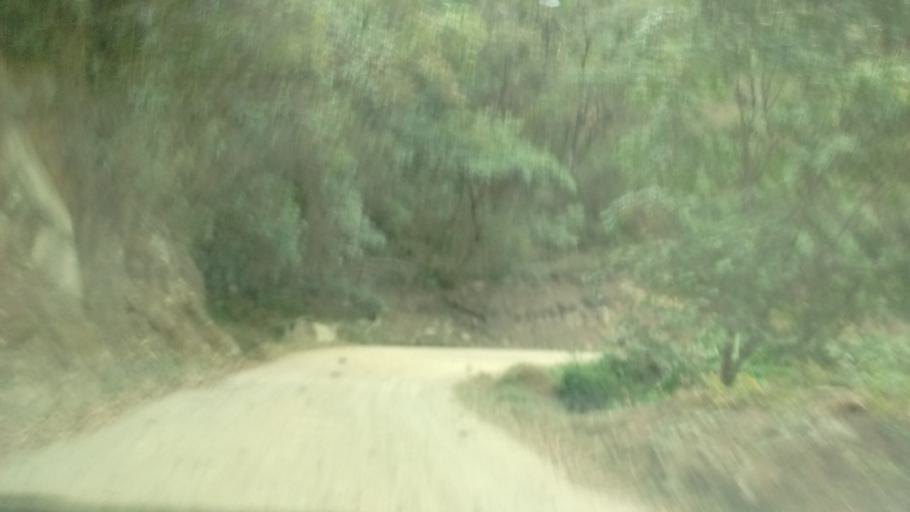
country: CO
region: Cauca
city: La Vega
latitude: 2.0363
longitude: -76.7968
